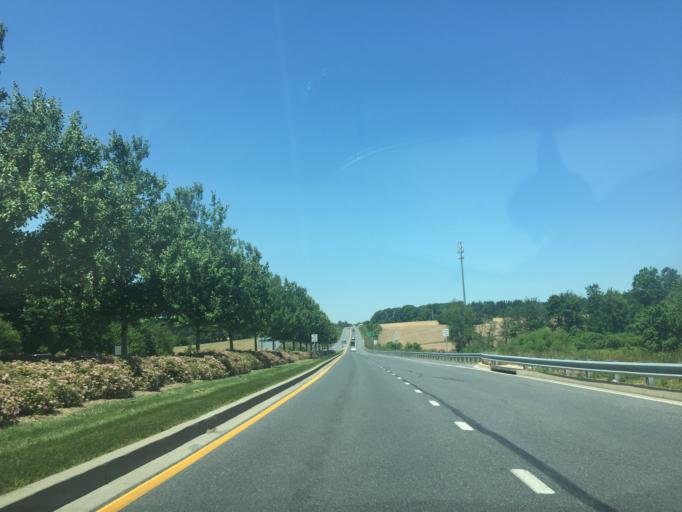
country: US
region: Maryland
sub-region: Carroll County
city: Hampstead
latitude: 39.5822
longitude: -76.8434
